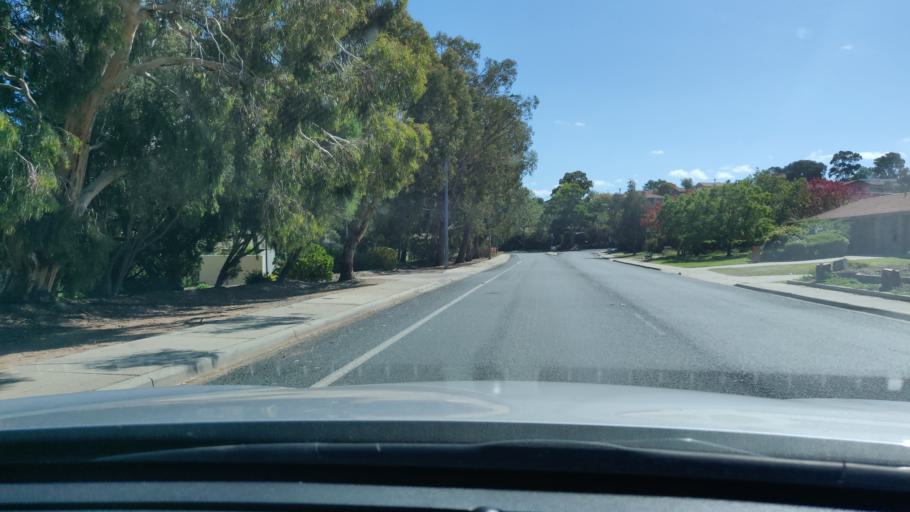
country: AU
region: Australian Capital Territory
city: Macarthur
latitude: -35.4371
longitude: 149.0977
